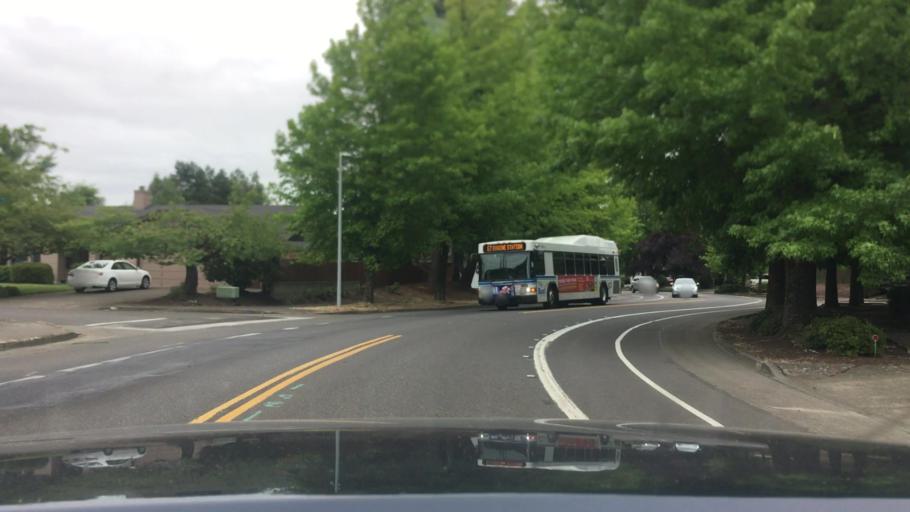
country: US
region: Oregon
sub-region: Lane County
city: Eugene
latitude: 44.0932
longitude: -123.0850
